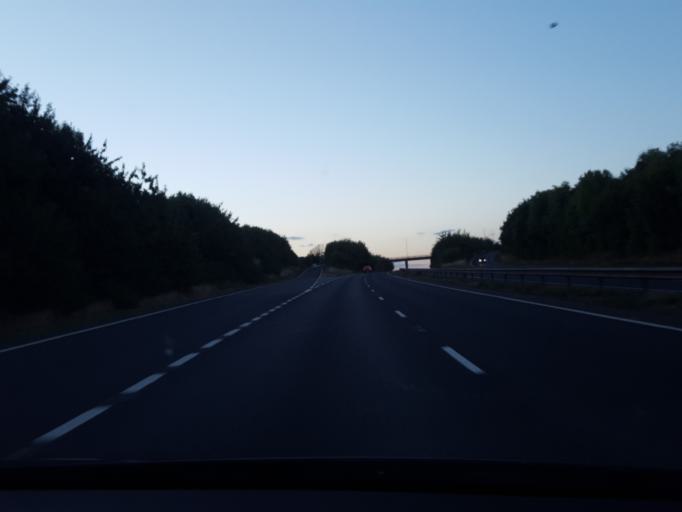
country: GB
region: England
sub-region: Leicestershire
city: Mountsorrel
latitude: 52.7163
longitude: -1.1263
